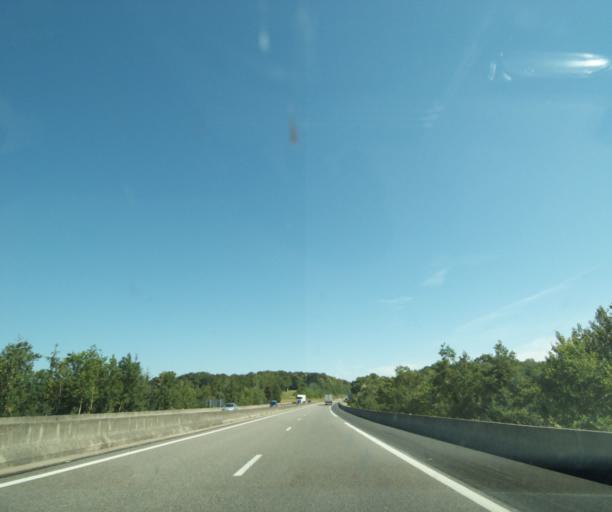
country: FR
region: Lorraine
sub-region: Departement des Vosges
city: Bulgneville
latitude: 48.2402
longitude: 5.8611
